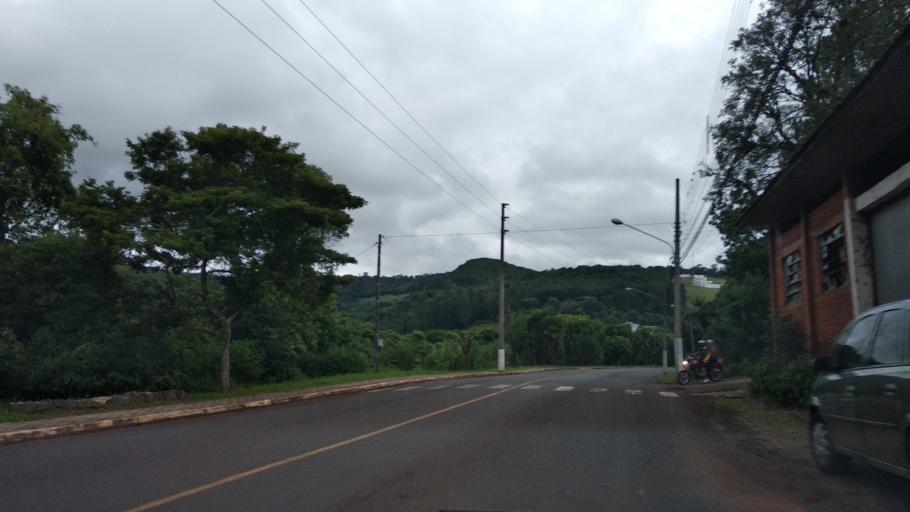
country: BR
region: Santa Catarina
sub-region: Videira
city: Videira
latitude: -27.0501
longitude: -51.2322
